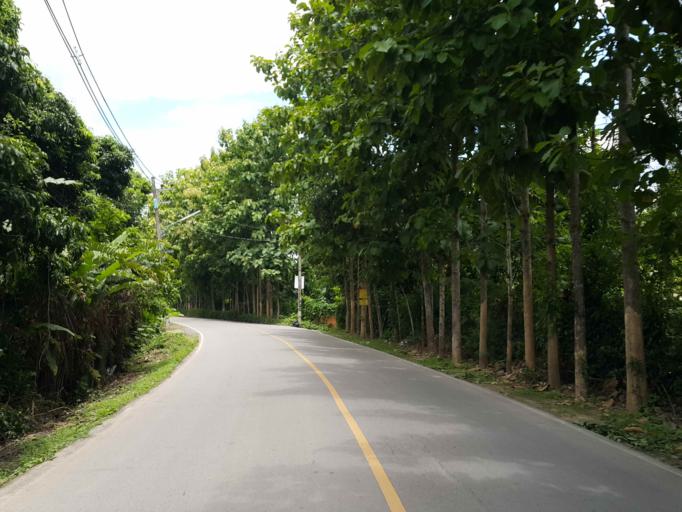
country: TH
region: Chiang Mai
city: San Sai
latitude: 18.8587
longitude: 98.9850
